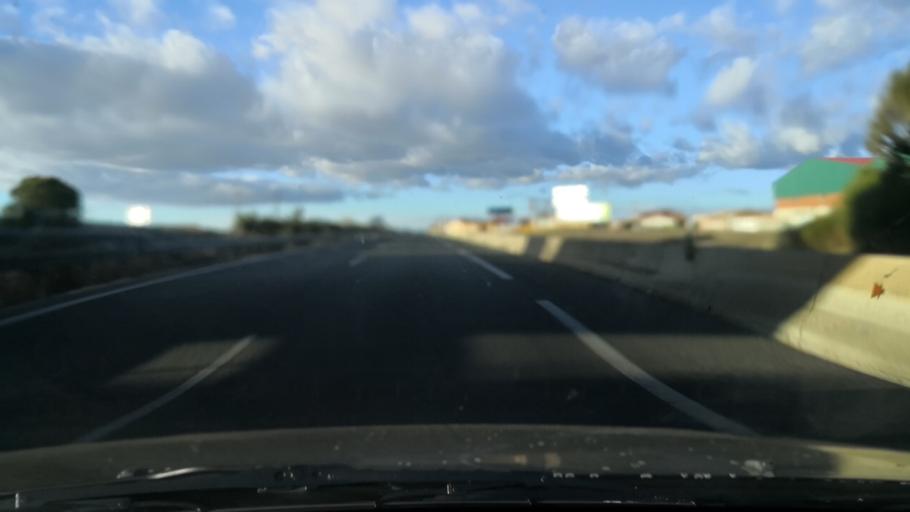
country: ES
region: Castille and Leon
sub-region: Provincia de Valladolid
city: Ataquines
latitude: 41.1777
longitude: -4.8056
